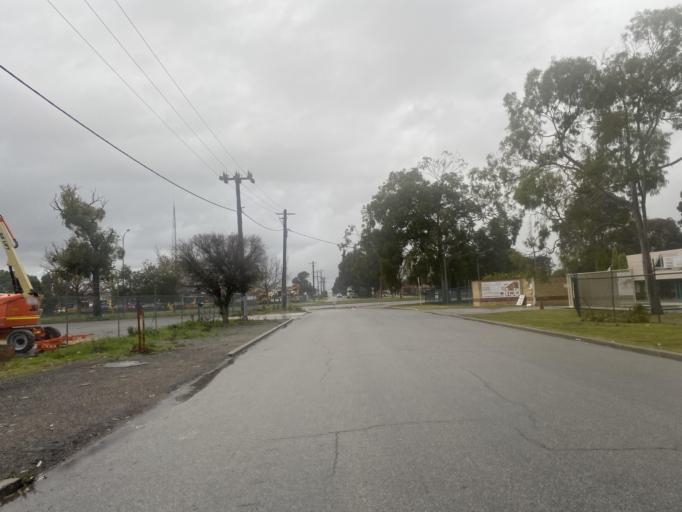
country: AU
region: Western Australia
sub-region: Canning
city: Queens Park
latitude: -31.9967
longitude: 115.9575
